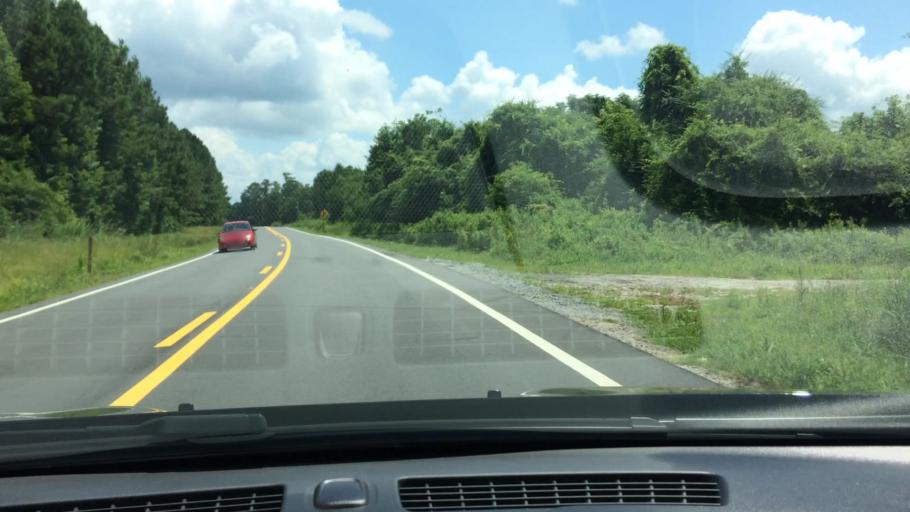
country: US
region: North Carolina
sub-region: Craven County
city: Vanceboro
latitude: 35.4297
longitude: -77.1800
